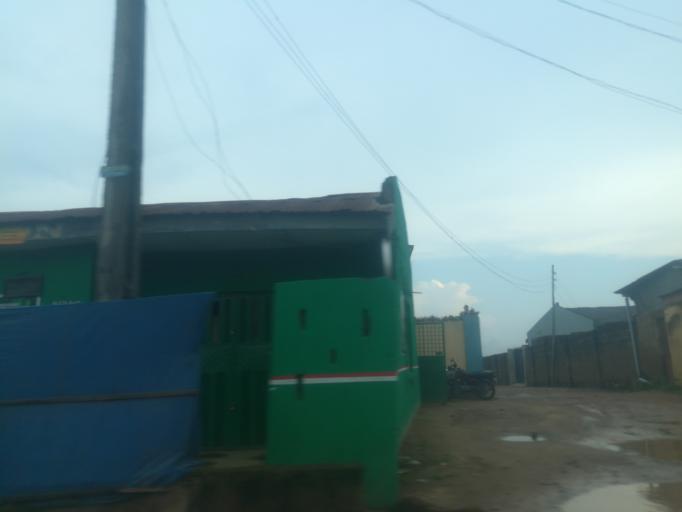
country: NG
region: Oyo
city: Ibadan
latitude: 7.3540
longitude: 3.8264
